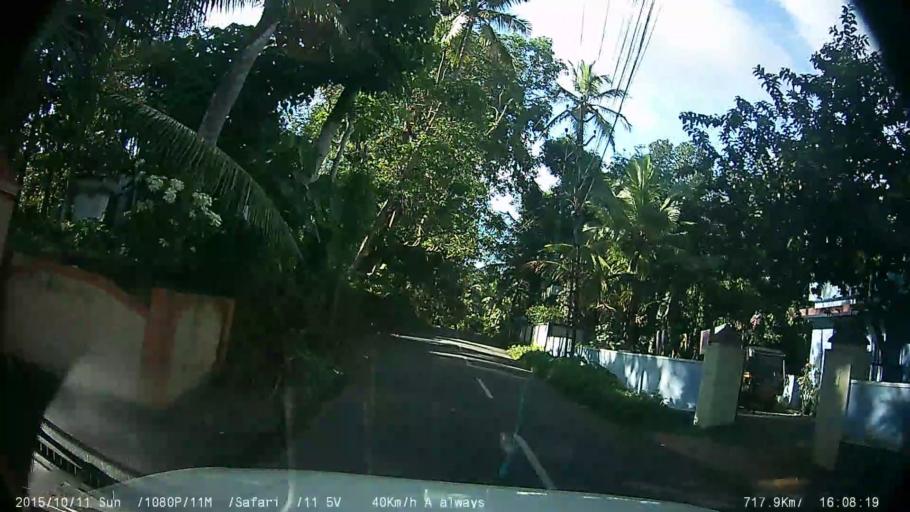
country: IN
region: Kerala
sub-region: Kottayam
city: Palackattumala
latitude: 9.6885
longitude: 76.6101
